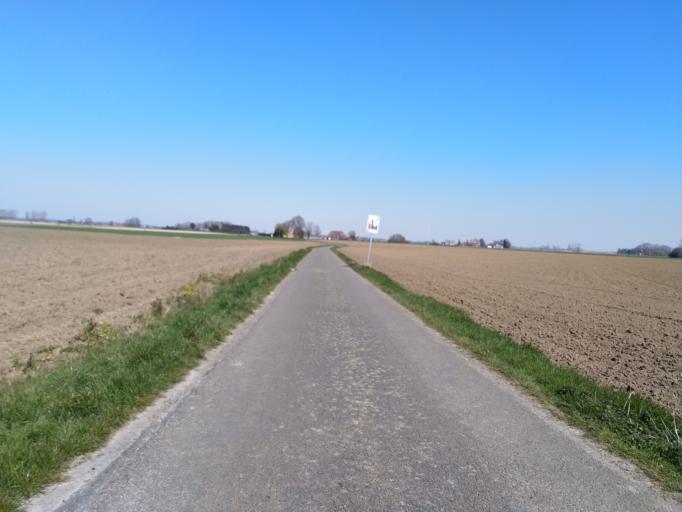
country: BE
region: Wallonia
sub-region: Province du Hainaut
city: Jurbise
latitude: 50.5390
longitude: 3.9156
